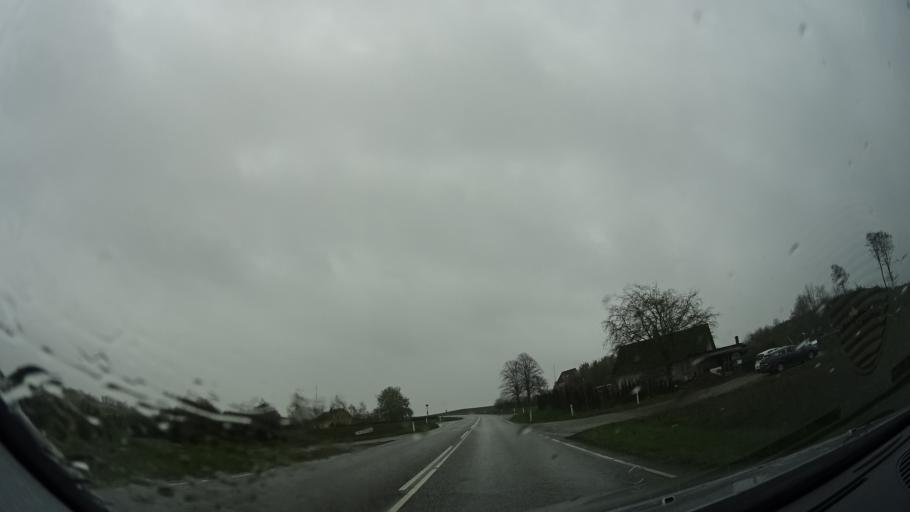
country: DK
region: Zealand
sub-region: Odsherred Kommune
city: Asnaes
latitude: 55.8133
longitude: 11.5852
